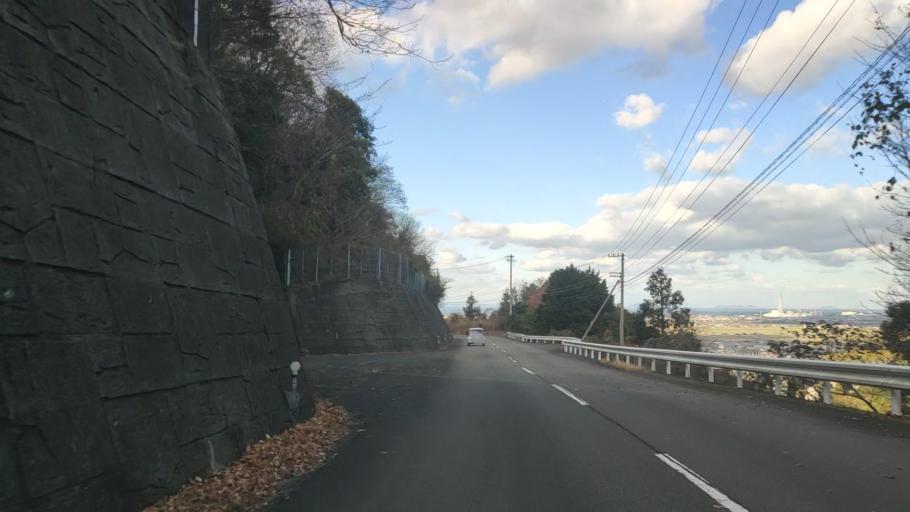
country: JP
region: Ehime
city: Saijo
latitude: 33.8821
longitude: 133.1326
